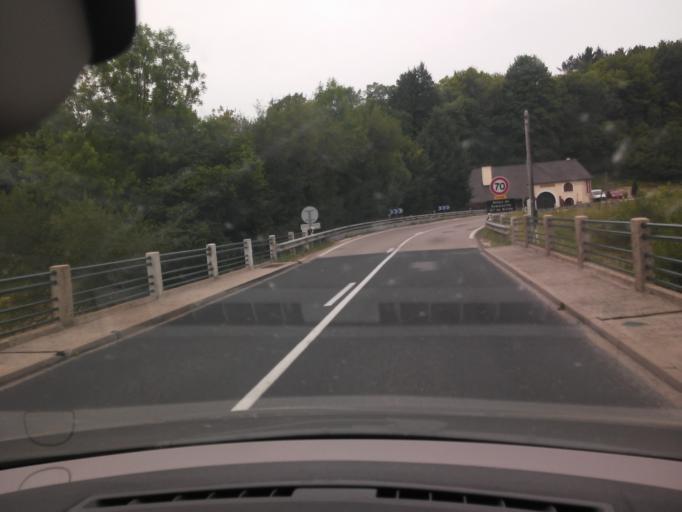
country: FR
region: Lorraine
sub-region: Departement de la Meuse
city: Saint-Mihiel
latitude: 48.8684
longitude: 5.5180
